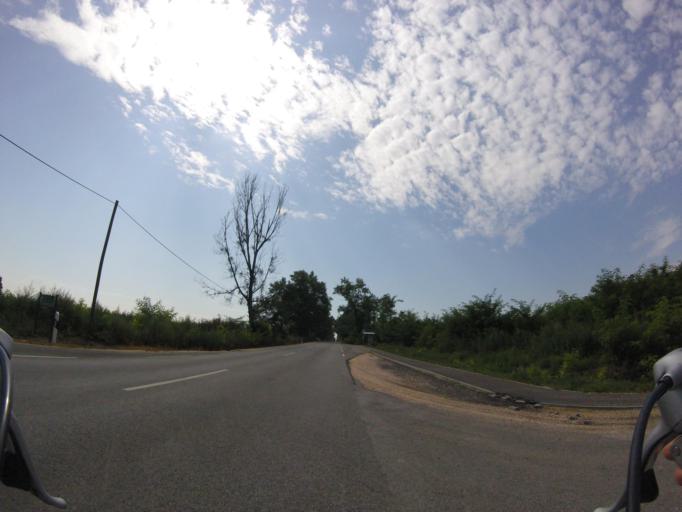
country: HU
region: Komarom-Esztergom
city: Kornye
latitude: 47.5823
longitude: 18.3228
